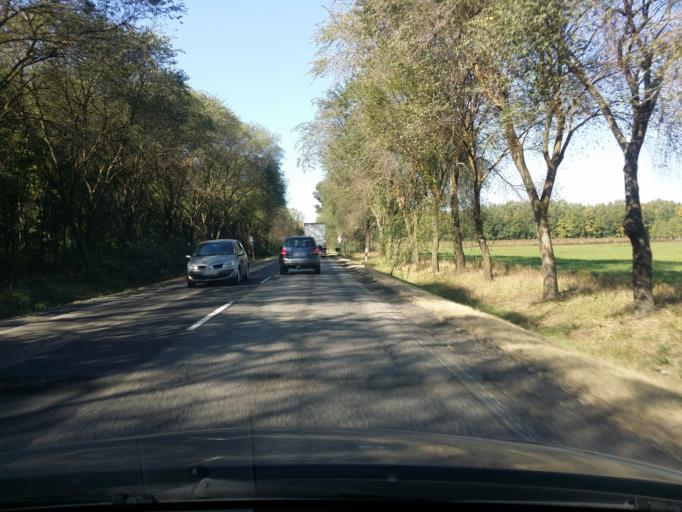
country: HU
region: Bacs-Kiskun
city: Nyarlorinc
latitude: 46.8990
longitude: 19.8215
